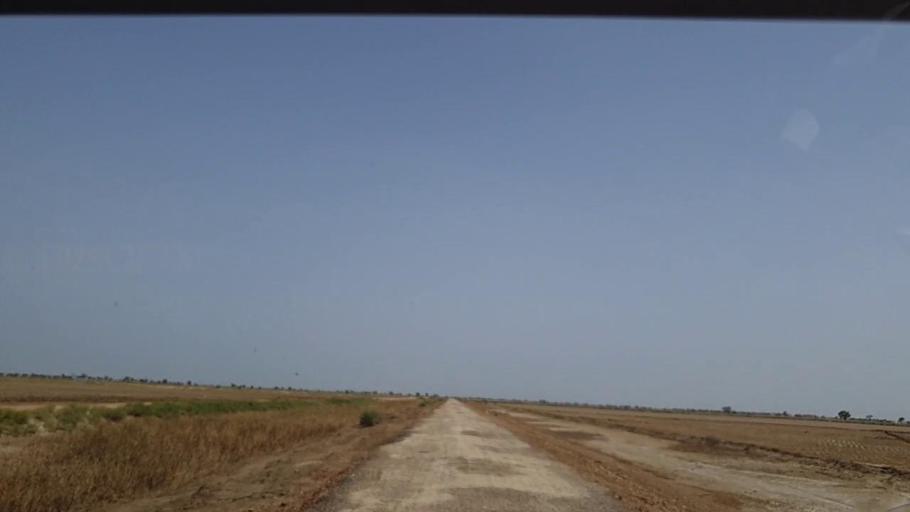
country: PK
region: Sindh
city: Johi
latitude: 26.7870
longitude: 67.6453
